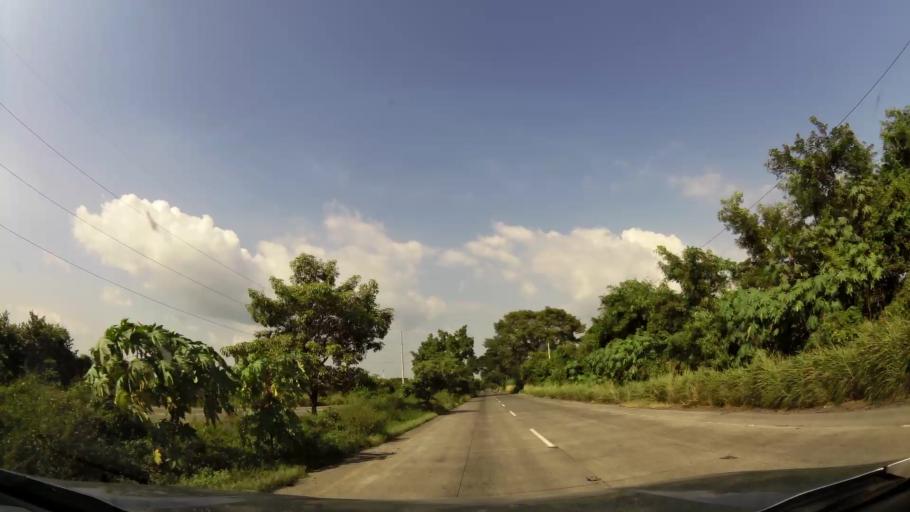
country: GT
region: Escuintla
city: Puerto San Jose
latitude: 14.0012
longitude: -90.7871
